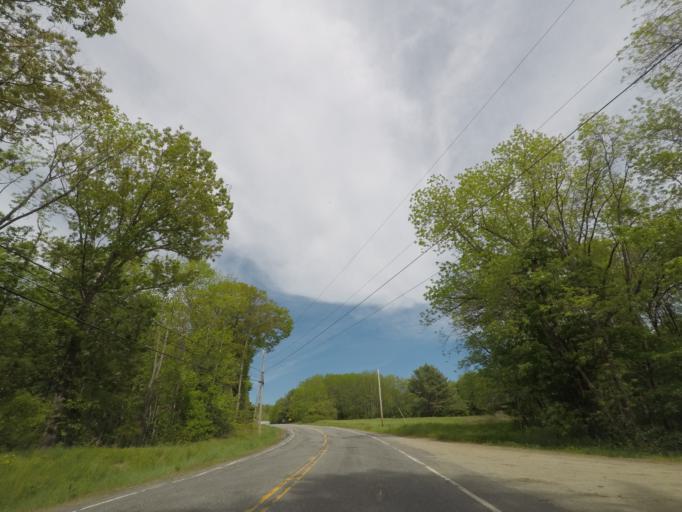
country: US
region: Maine
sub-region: Sagadahoc County
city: Richmond
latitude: 44.0837
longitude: -69.7468
